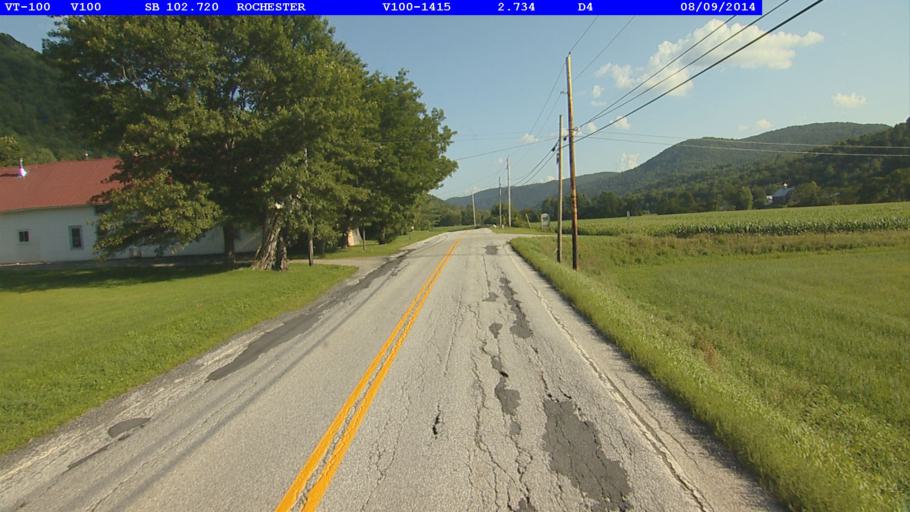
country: US
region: Vermont
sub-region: Orange County
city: Randolph
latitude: 43.8413
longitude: -72.7974
